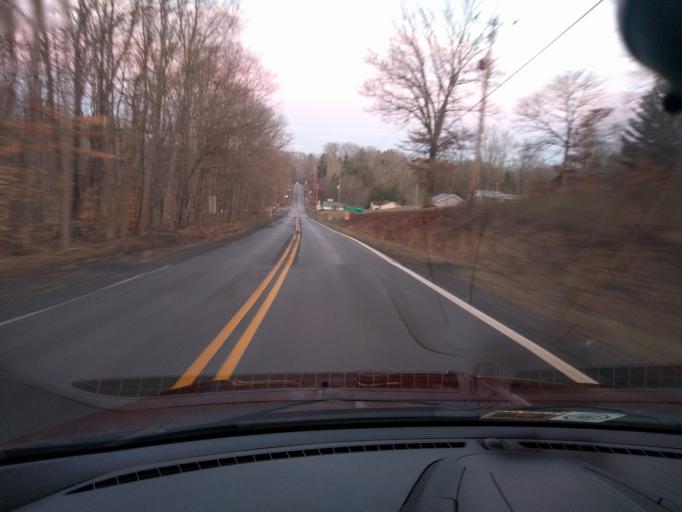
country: US
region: West Virginia
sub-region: Greenbrier County
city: Rainelle
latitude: 38.0194
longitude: -80.9102
